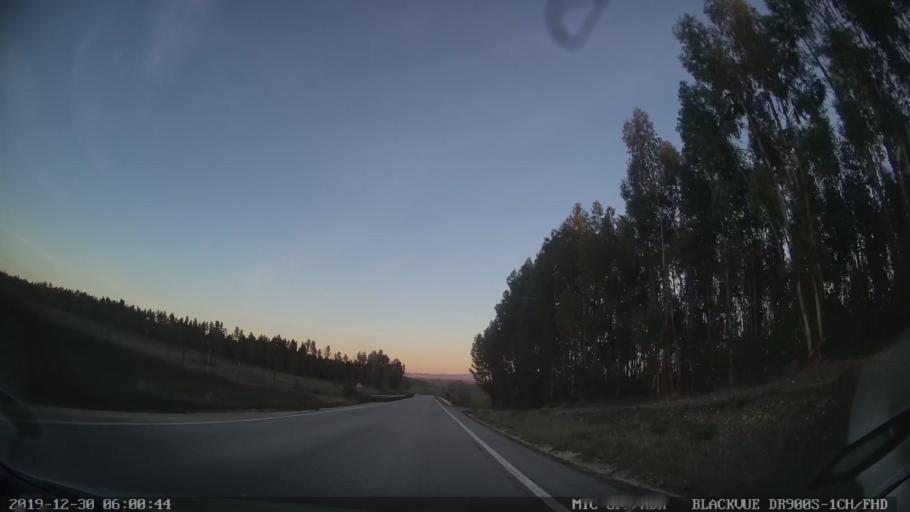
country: PT
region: Castelo Branco
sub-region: Idanha-A-Nova
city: Idanha-a-Nova
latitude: 40.0546
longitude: -7.2454
